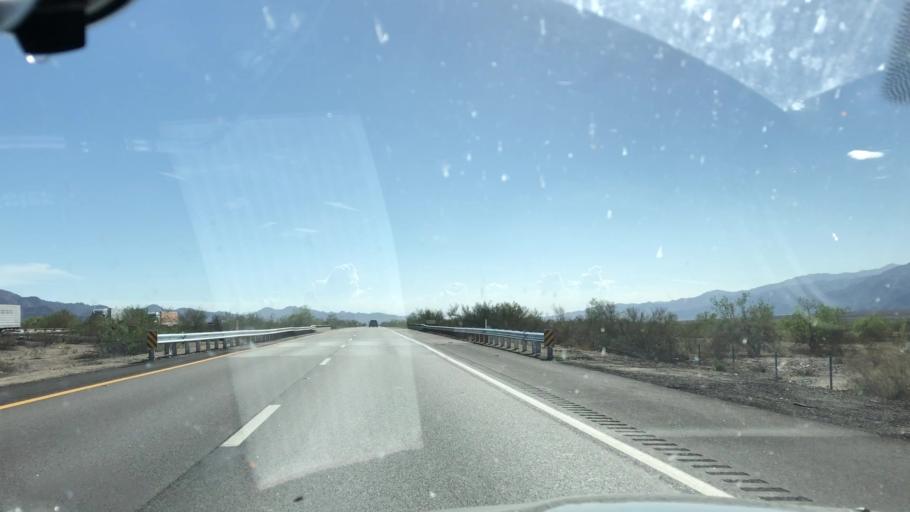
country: US
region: California
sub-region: Imperial County
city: Niland
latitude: 33.6872
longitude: -115.5218
